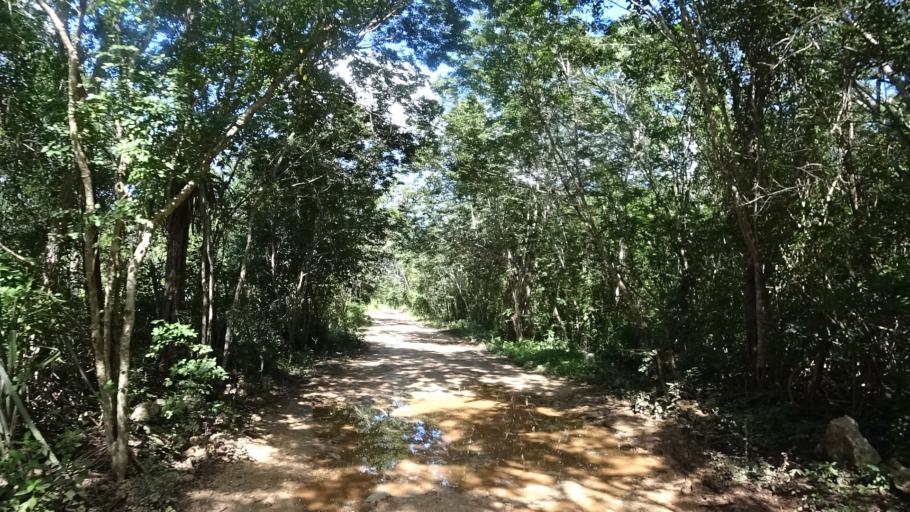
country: MX
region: Yucatan
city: Sacalum
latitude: 20.6385
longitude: -89.6321
